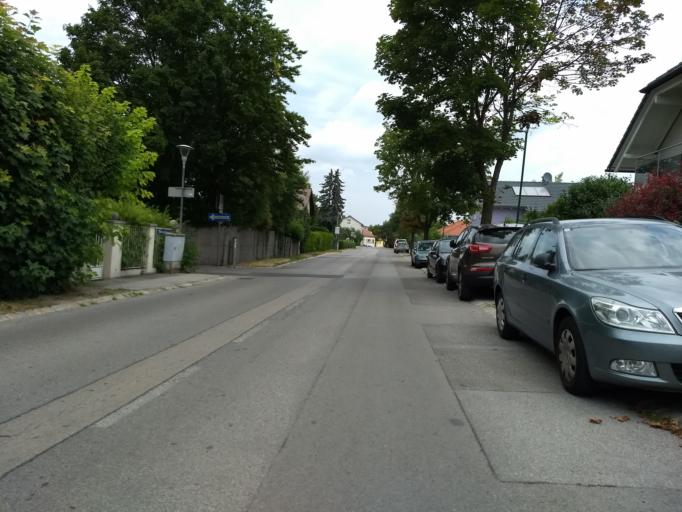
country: AT
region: Lower Austria
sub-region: Politischer Bezirk Modling
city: Guntramsdorf
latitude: 48.0423
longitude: 16.3112
